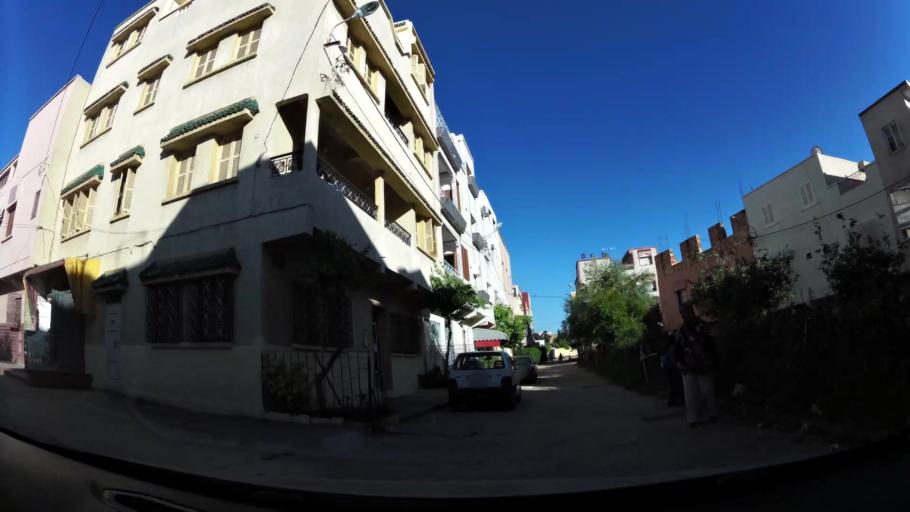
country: MA
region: Meknes-Tafilalet
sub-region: Meknes
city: Meknes
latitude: 33.8787
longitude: -5.5623
